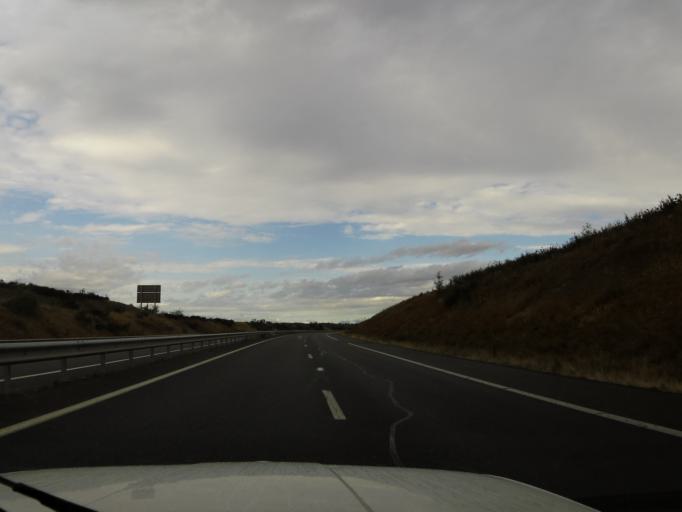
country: FR
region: Rhone-Alpes
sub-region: Departement de l'Isere
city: Grenay
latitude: 45.6980
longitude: 5.0933
